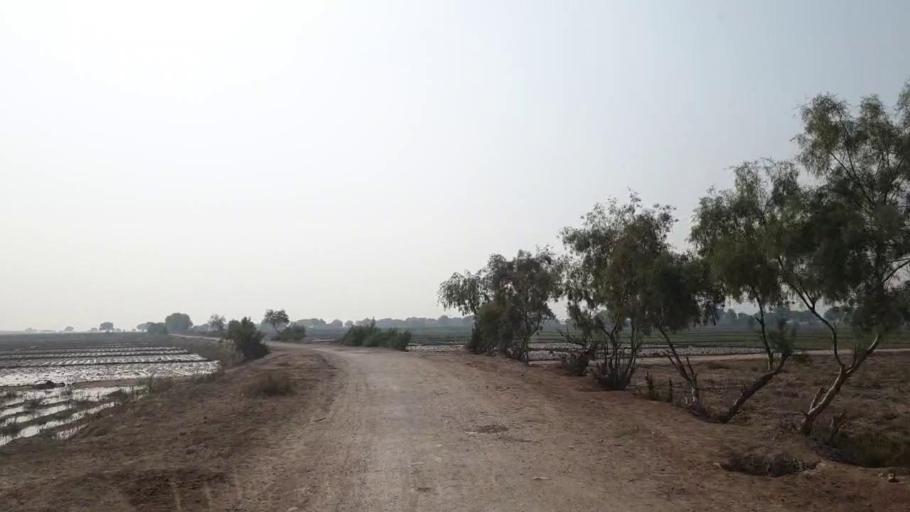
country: PK
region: Sindh
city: Bhan
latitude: 26.4704
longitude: 67.7388
